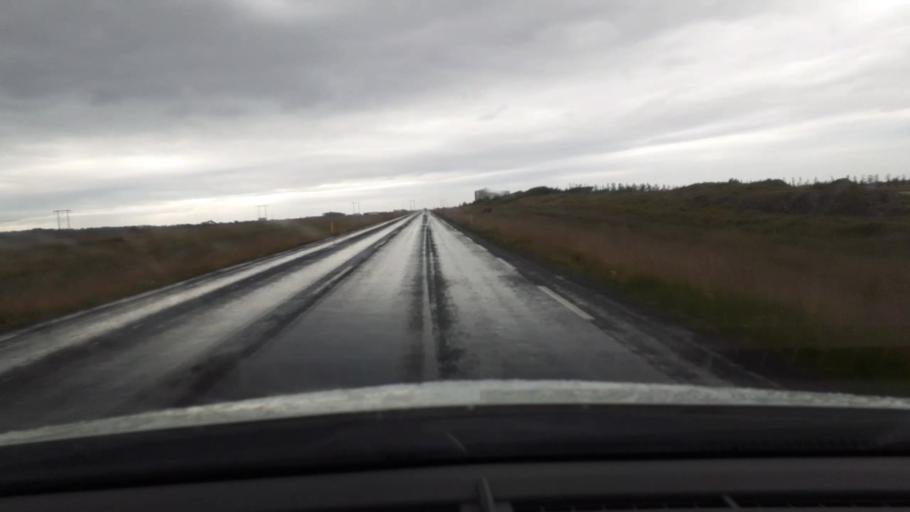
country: IS
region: West
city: Akranes
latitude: 64.3362
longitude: -22.0279
